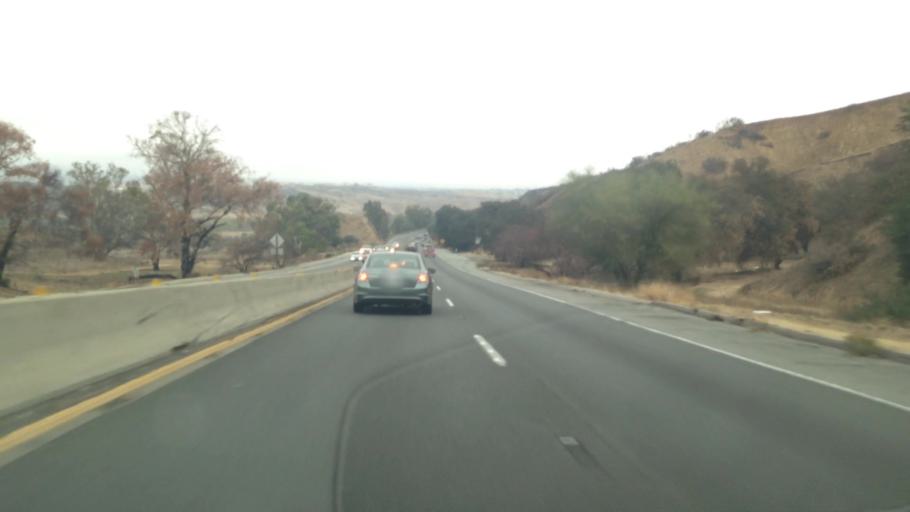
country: US
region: California
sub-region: Riverside County
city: Calimesa
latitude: 33.9462
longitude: -117.0676
